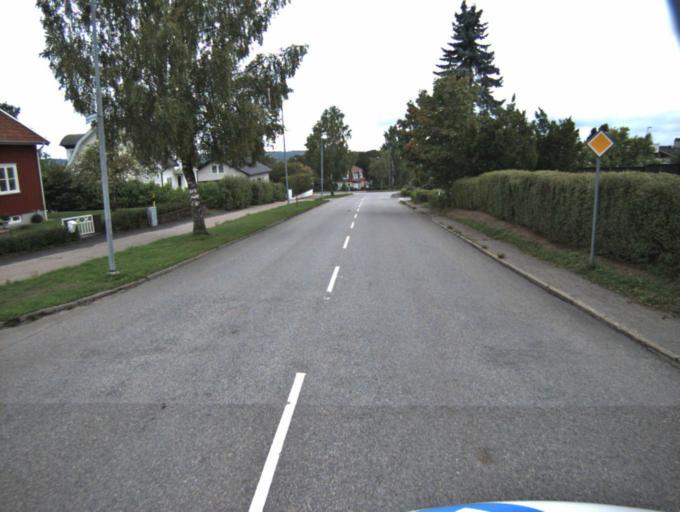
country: SE
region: Vaestra Goetaland
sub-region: Ulricehamns Kommun
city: Ulricehamn
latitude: 57.7845
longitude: 13.4243
